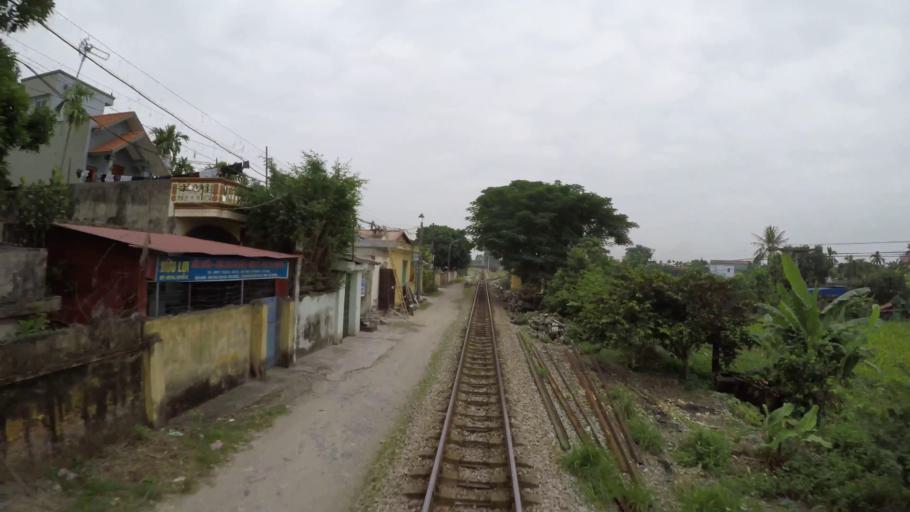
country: VN
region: Hai Phong
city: An Duong
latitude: 20.9081
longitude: 106.5728
